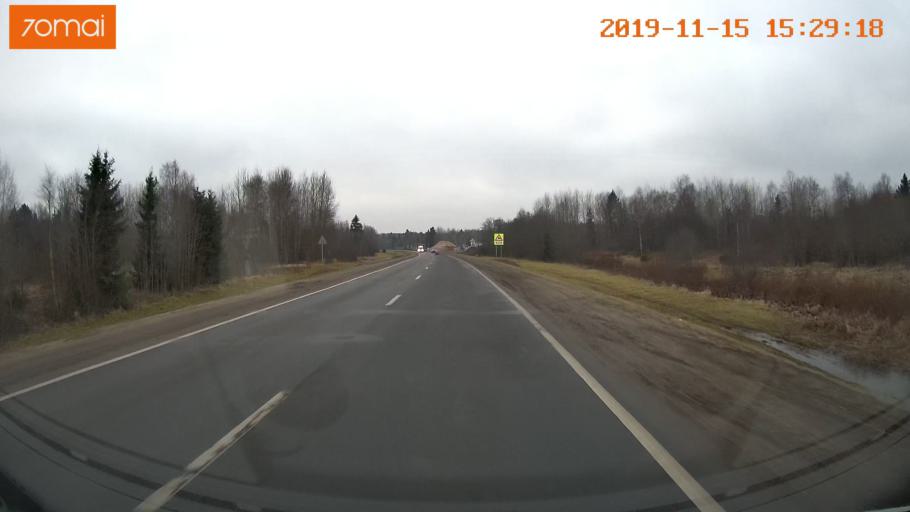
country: RU
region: Jaroslavl
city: Danilov
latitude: 58.1222
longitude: 40.1217
